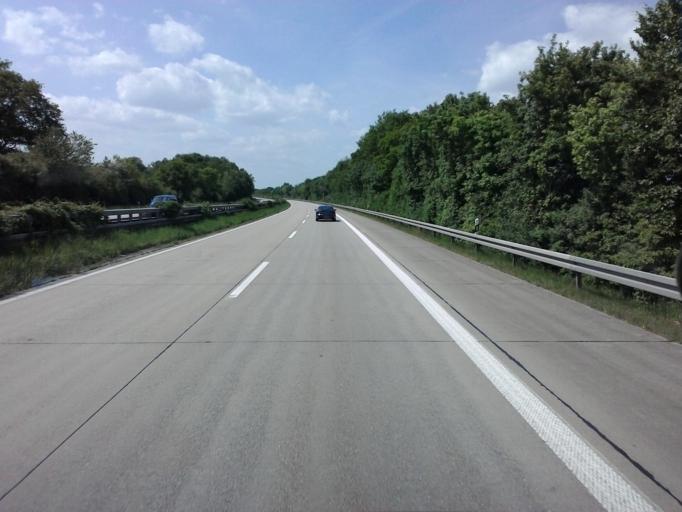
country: DE
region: North Rhine-Westphalia
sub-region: Regierungsbezirk Dusseldorf
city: Goch
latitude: 51.6744
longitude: 6.1062
